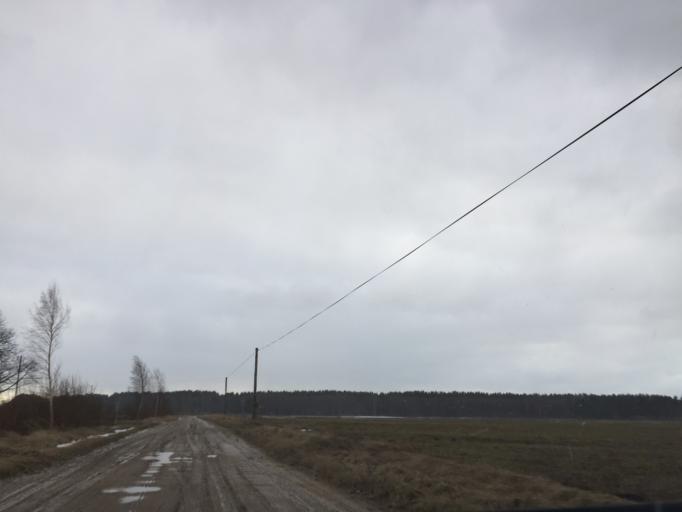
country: LV
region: Salacgrivas
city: Salacgriva
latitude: 57.6446
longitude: 24.3899
